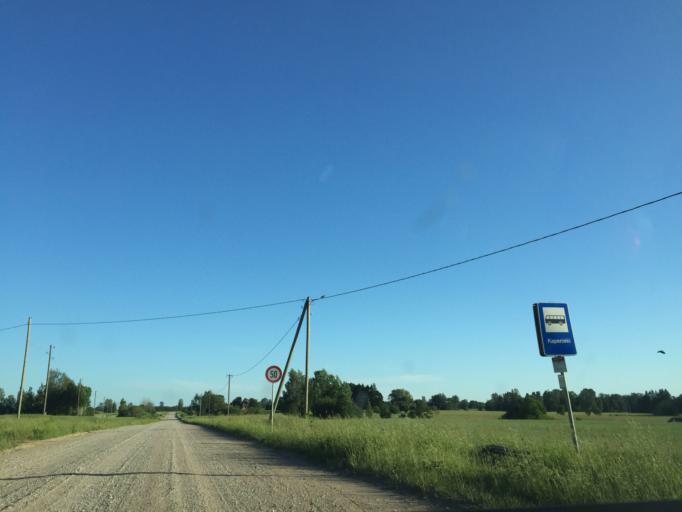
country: LV
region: Broceni
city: Broceni
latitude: 56.8196
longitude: 22.5465
